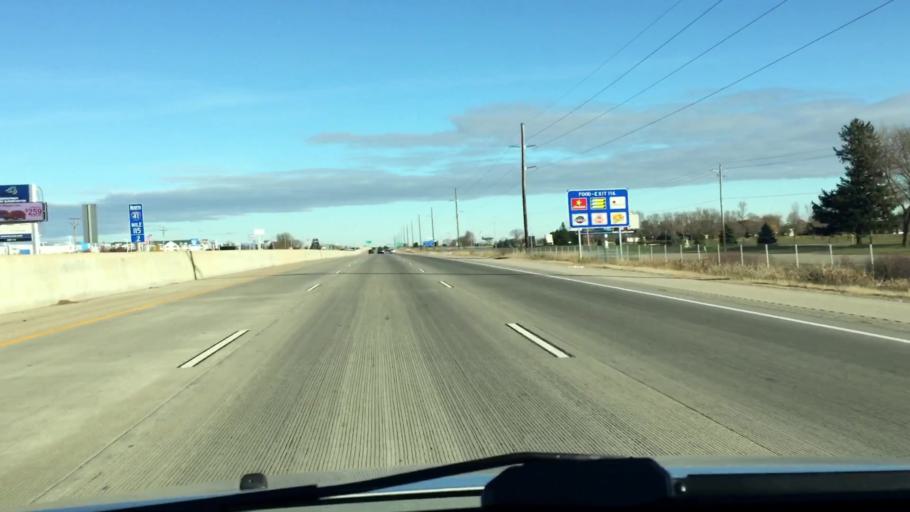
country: US
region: Wisconsin
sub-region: Winnebago County
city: Oshkosh
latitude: 43.9748
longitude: -88.5828
